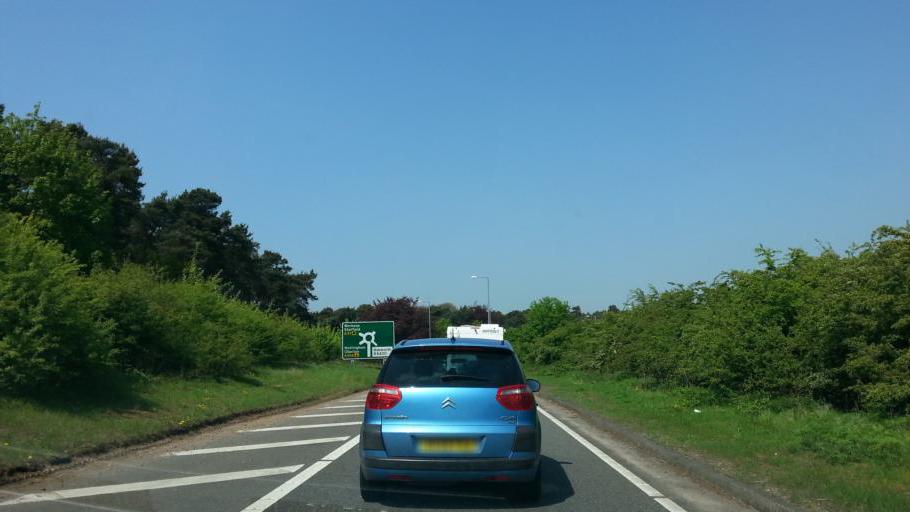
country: GB
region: England
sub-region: Nottinghamshire
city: Babworth
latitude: 53.2952
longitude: -1.0303
